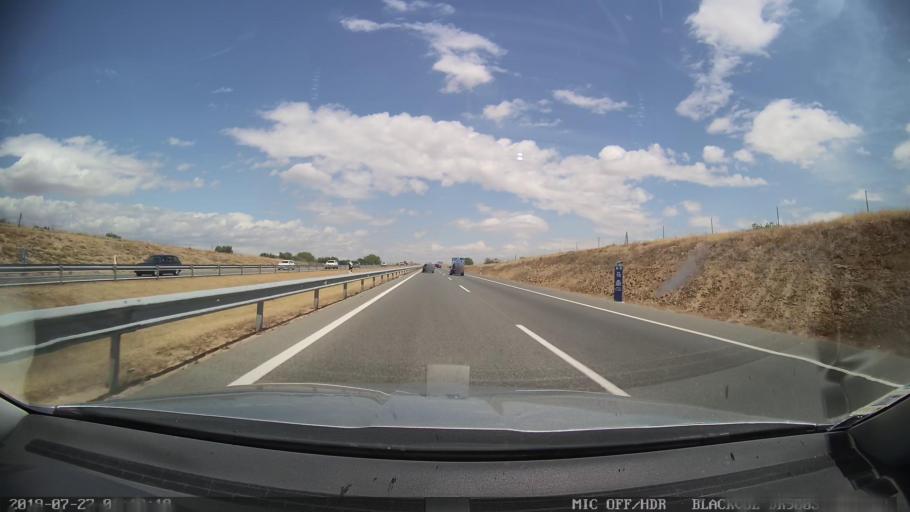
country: ES
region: Castille-La Mancha
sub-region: Province of Toledo
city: Quismondo
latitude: 40.0914
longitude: -4.3436
